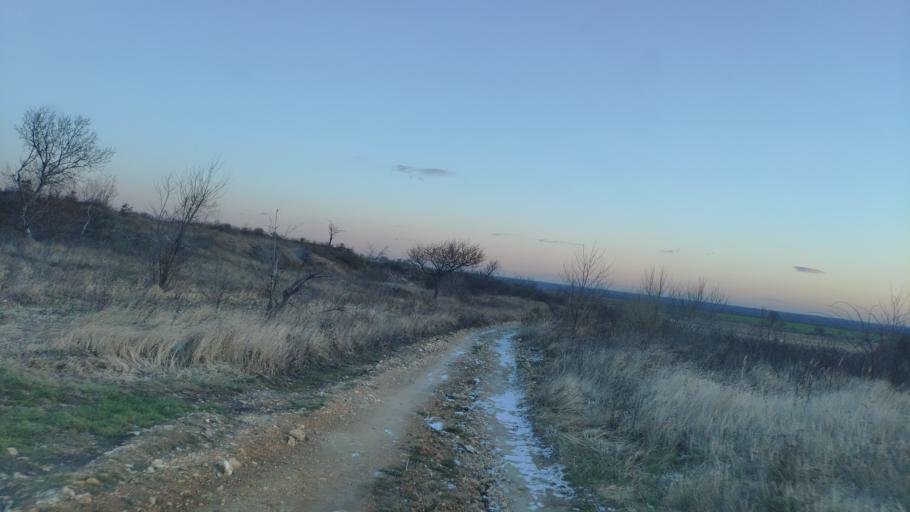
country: HU
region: Borsod-Abauj-Zemplen
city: Olaszliszka
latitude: 48.2699
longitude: 21.3993
